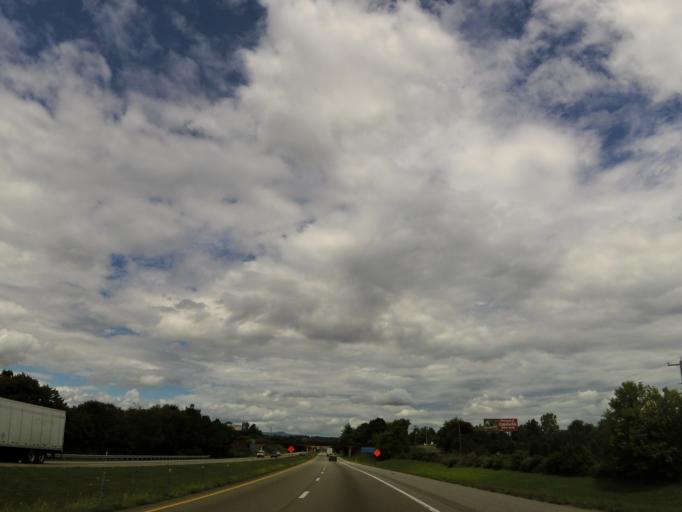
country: US
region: Tennessee
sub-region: Anderson County
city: Norris
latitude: 36.1566
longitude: -84.0695
